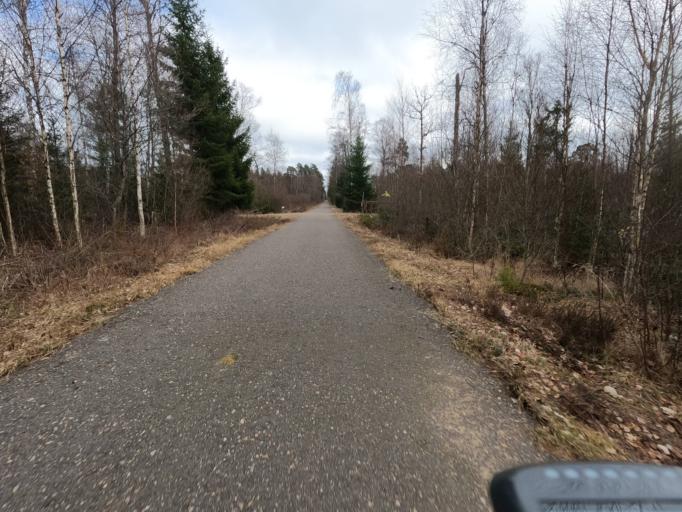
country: SE
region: Joenkoeping
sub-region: Varnamo Kommun
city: Rydaholm
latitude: 56.8499
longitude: 14.2010
